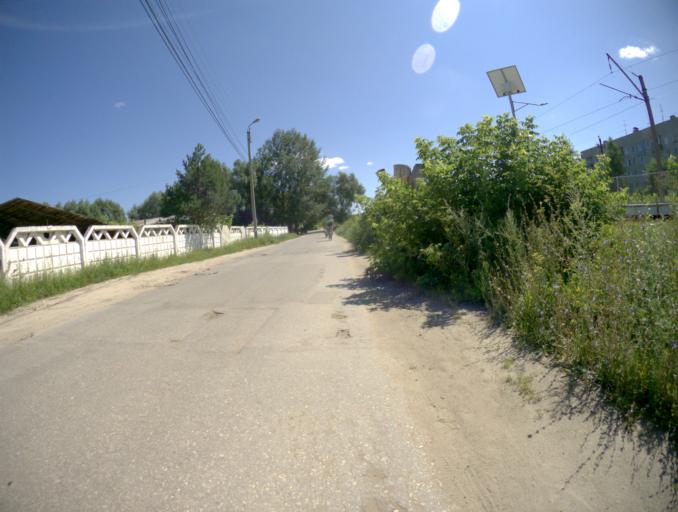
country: RU
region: Nizjnij Novgorod
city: Bor
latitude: 56.3664
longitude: 44.0609
